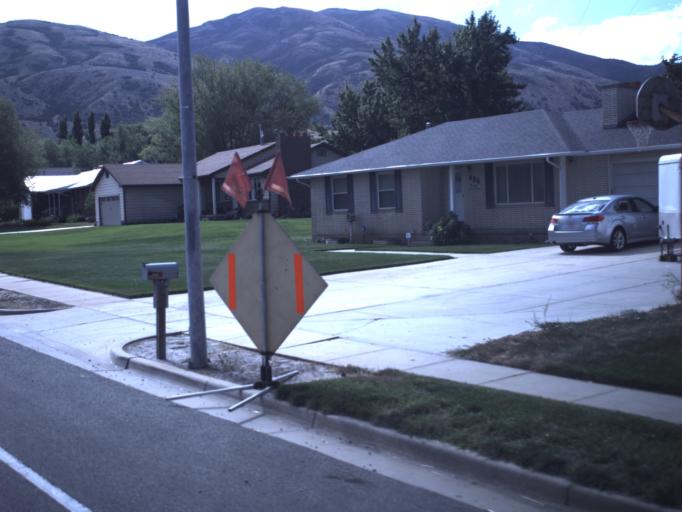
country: US
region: Utah
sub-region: Box Elder County
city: Brigham City
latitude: 41.5054
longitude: -112.0028
